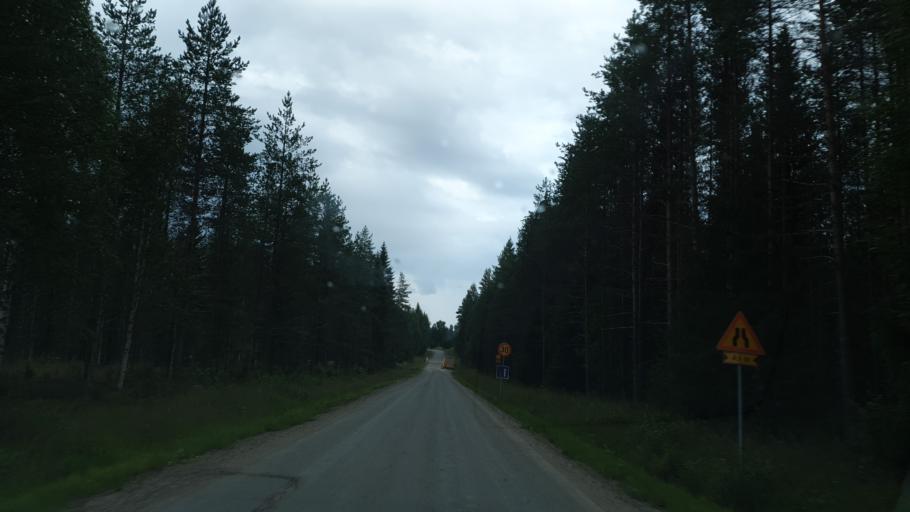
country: FI
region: Kainuu
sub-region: Kehys-Kainuu
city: Kuhmo
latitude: 64.2099
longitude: 29.3701
